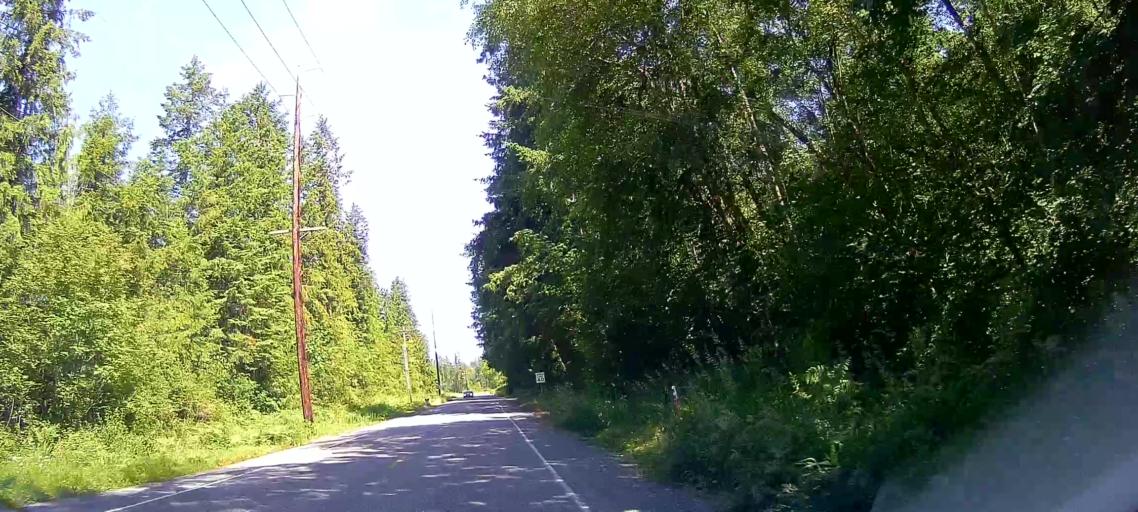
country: US
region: Washington
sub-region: Skagit County
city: Burlington
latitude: 48.5387
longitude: -122.3108
